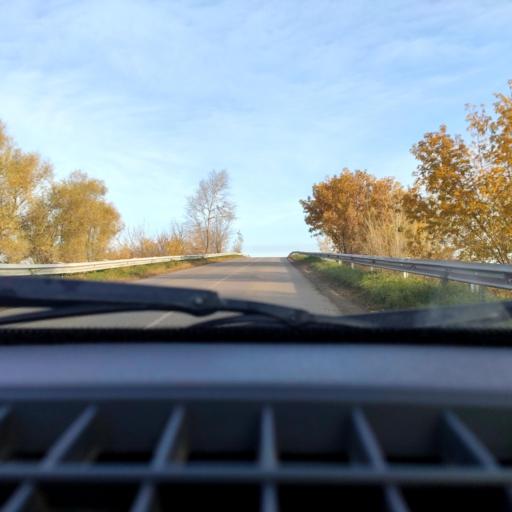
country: RU
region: Bashkortostan
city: Avdon
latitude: 54.6505
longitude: 55.7780
